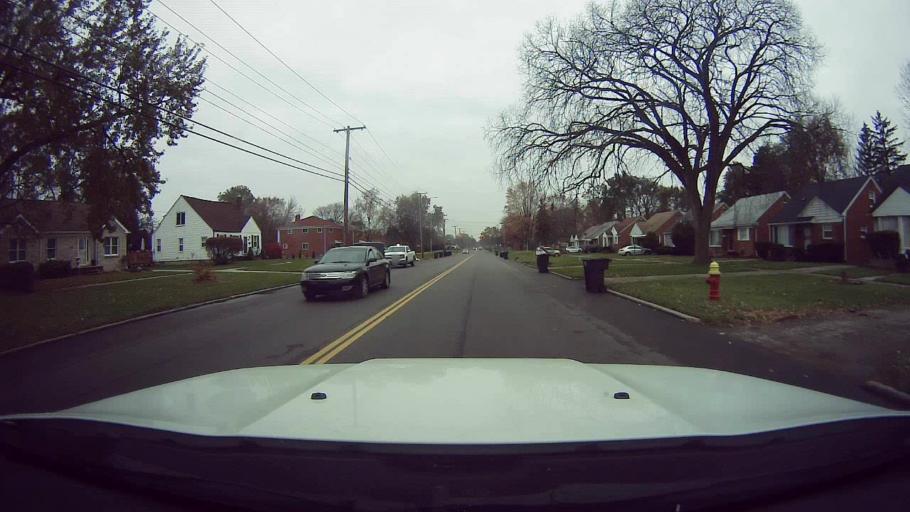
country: US
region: Michigan
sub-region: Oakland County
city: Southfield
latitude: 42.4415
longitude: -83.2393
